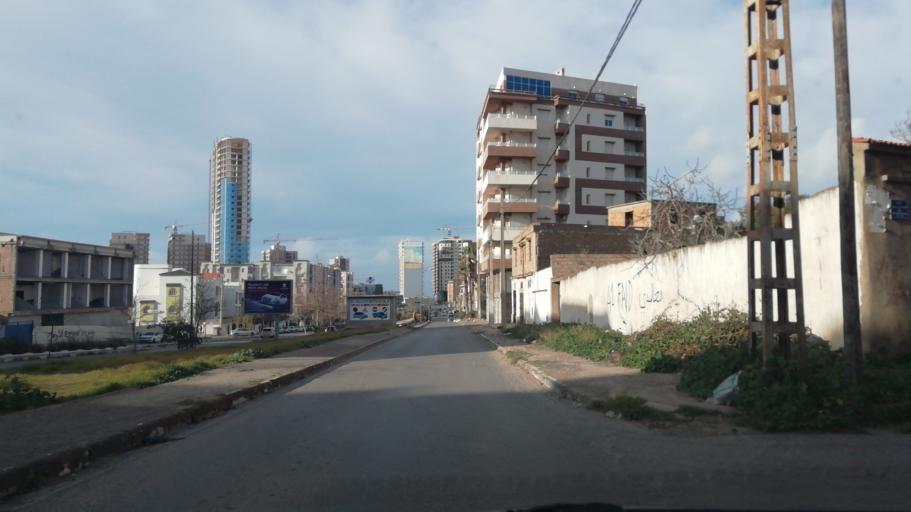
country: DZ
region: Oran
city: Bir el Djir
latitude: 35.7251
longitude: -0.5844
